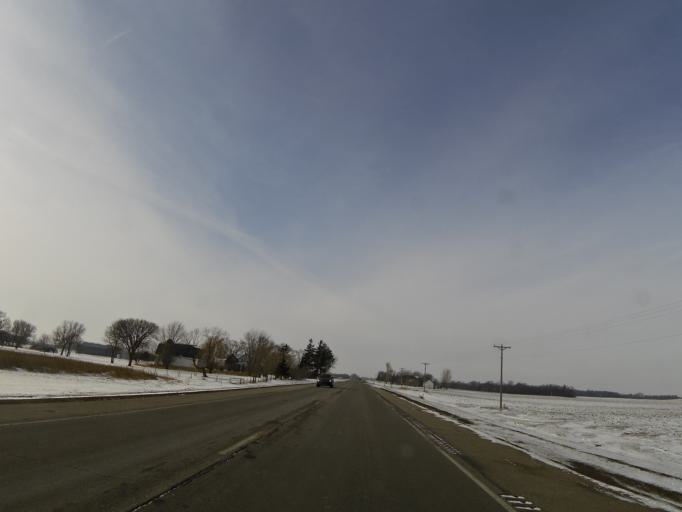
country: US
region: Minnesota
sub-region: McLeod County
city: Lester Prairie
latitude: 44.9067
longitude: -94.1550
